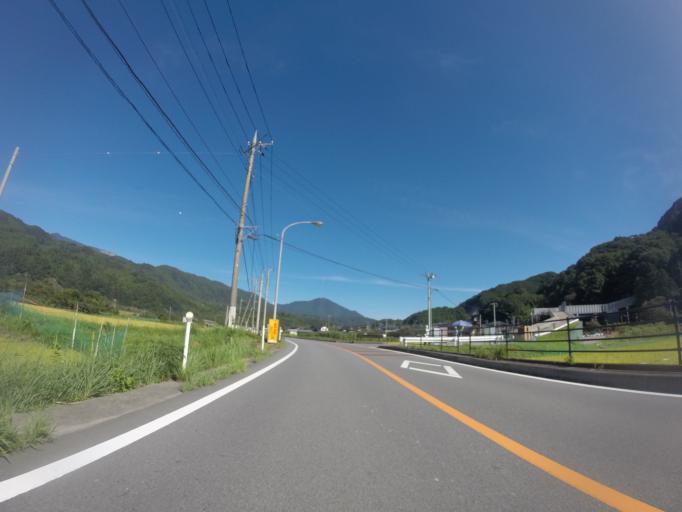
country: JP
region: Shizuoka
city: Fujinomiya
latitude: 35.3304
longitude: 138.4513
